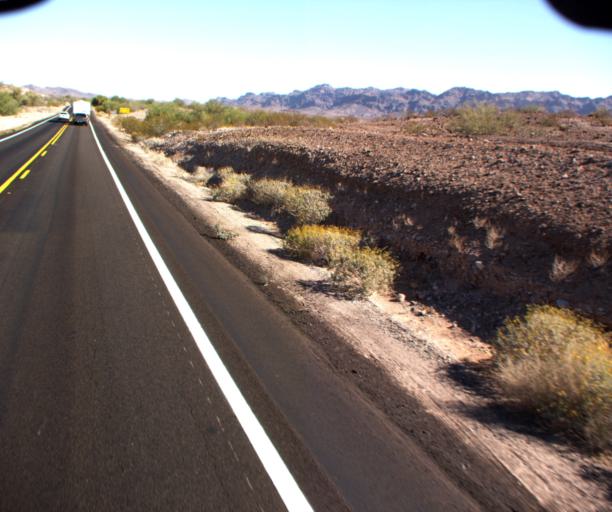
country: US
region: Arizona
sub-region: La Paz County
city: Quartzsite
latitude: 33.1624
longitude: -114.2792
